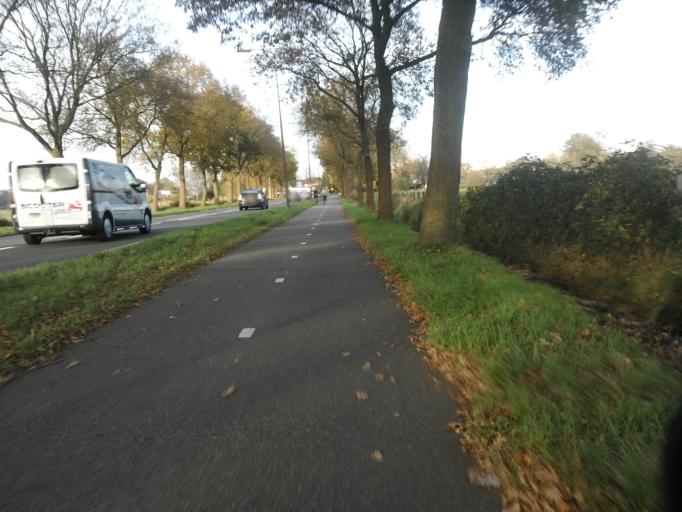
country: NL
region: Utrecht
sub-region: Gemeente Woudenberg
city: Woudenberg
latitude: 52.1038
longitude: 5.4141
